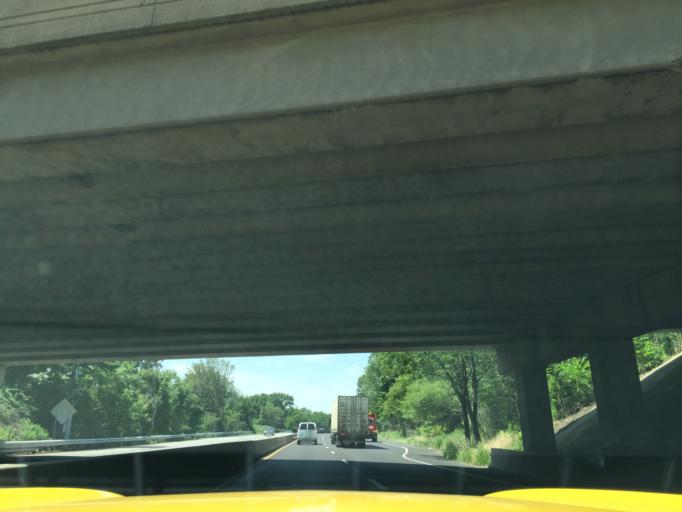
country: US
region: Pennsylvania
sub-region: Bucks County
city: Langhorne Manor
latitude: 40.1714
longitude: -74.9145
